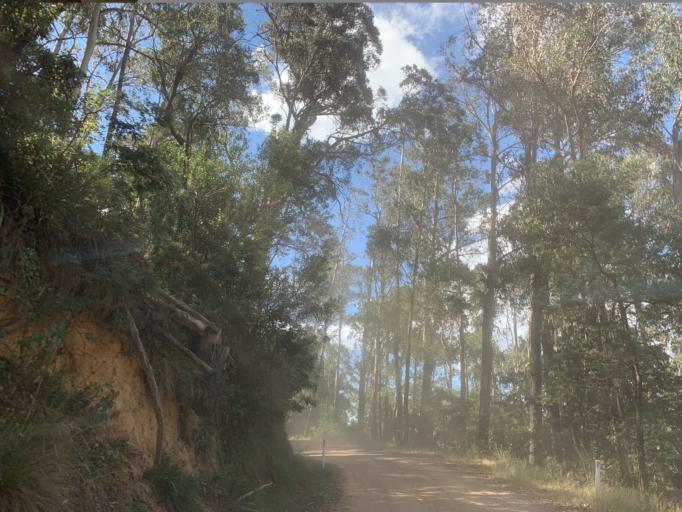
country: AU
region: Victoria
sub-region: Mansfield
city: Mansfield
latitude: -37.0924
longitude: 146.5187
